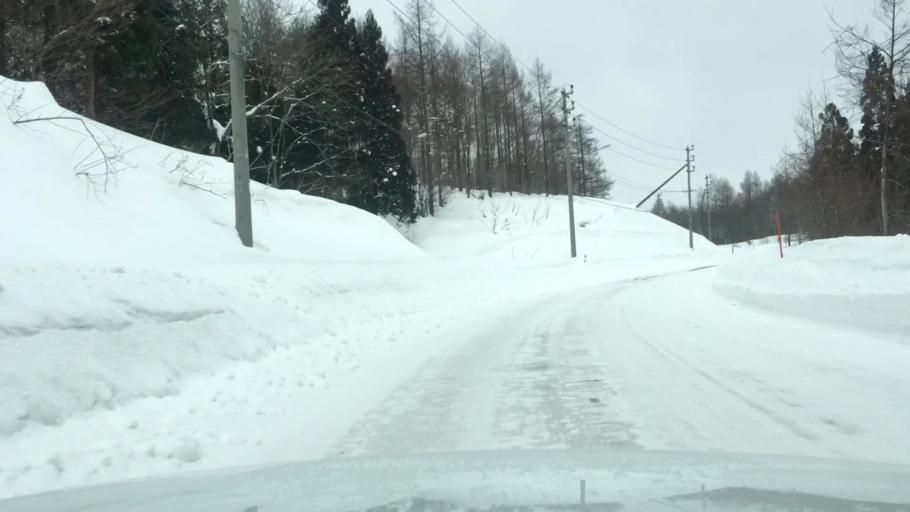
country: JP
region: Akita
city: Hanawa
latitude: 40.0006
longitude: 140.9860
